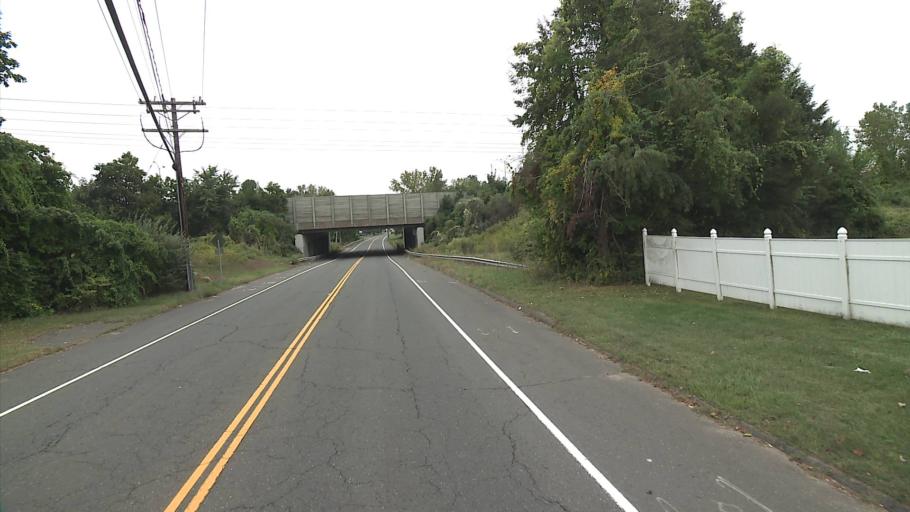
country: US
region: Connecticut
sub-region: Hartford County
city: Windsor Locks
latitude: 41.9196
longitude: -72.6160
